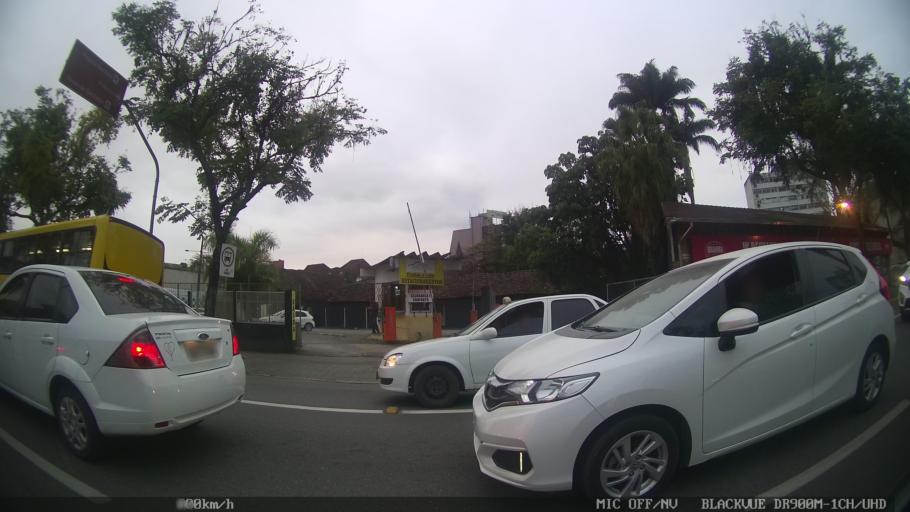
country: BR
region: Santa Catarina
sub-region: Joinville
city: Joinville
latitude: -26.3023
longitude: -48.8477
